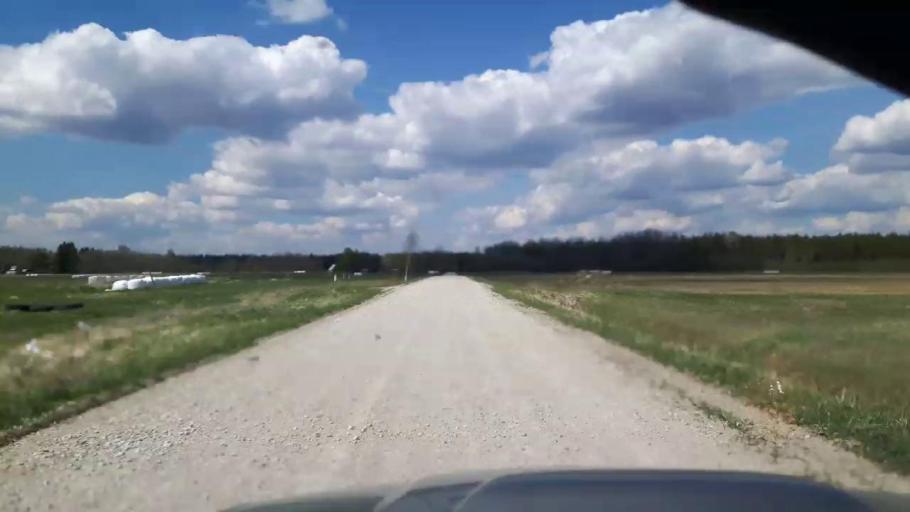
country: EE
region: Paernumaa
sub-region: Tootsi vald
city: Tootsi
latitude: 58.4622
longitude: 24.8710
